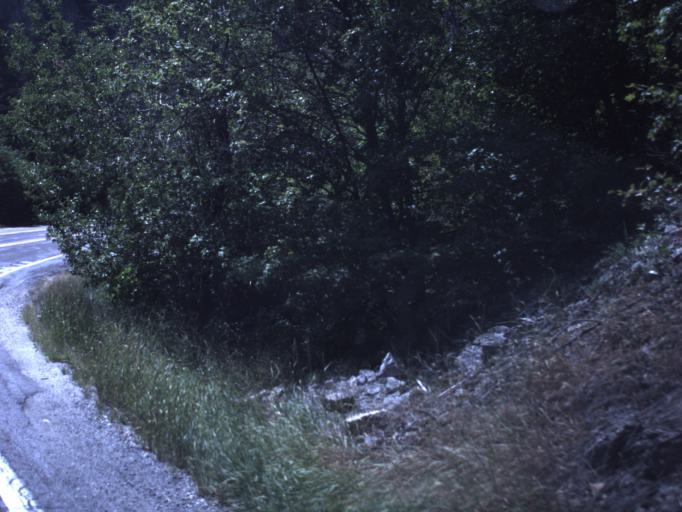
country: US
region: Utah
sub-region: Cache County
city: North Logan
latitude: 41.8142
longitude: -111.6188
